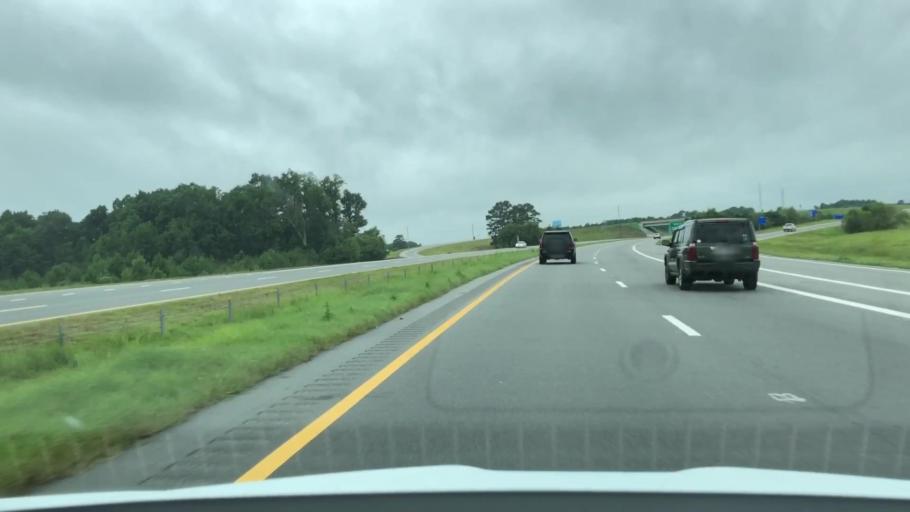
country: US
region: North Carolina
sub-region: Wayne County
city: Goldsboro
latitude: 35.4180
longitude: -77.9301
